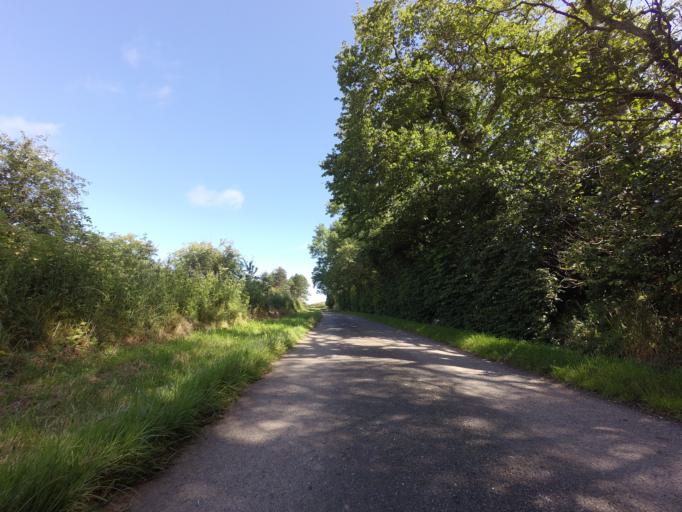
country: GB
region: Scotland
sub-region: Aberdeenshire
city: Banff
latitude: 57.6142
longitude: -2.5097
